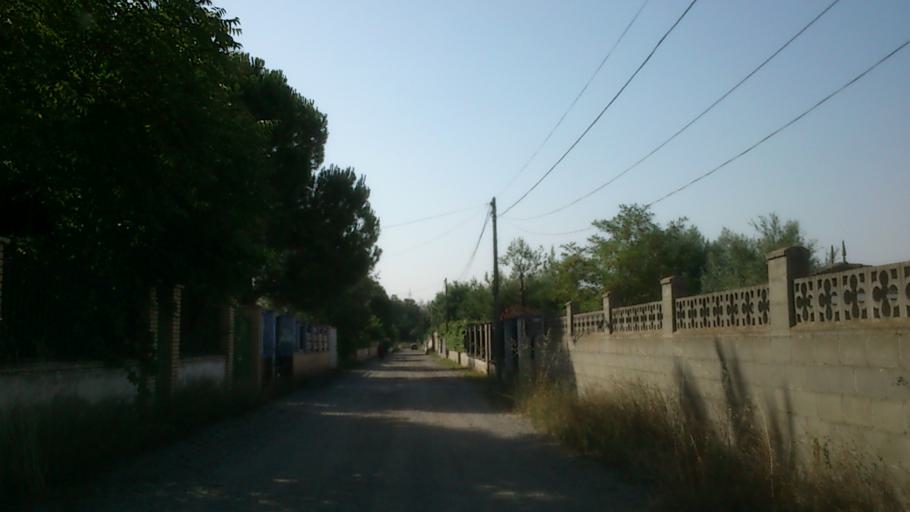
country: ES
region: Aragon
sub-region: Provincia de Zaragoza
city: Villanueva de Gallego
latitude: 41.7617
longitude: -0.8032
